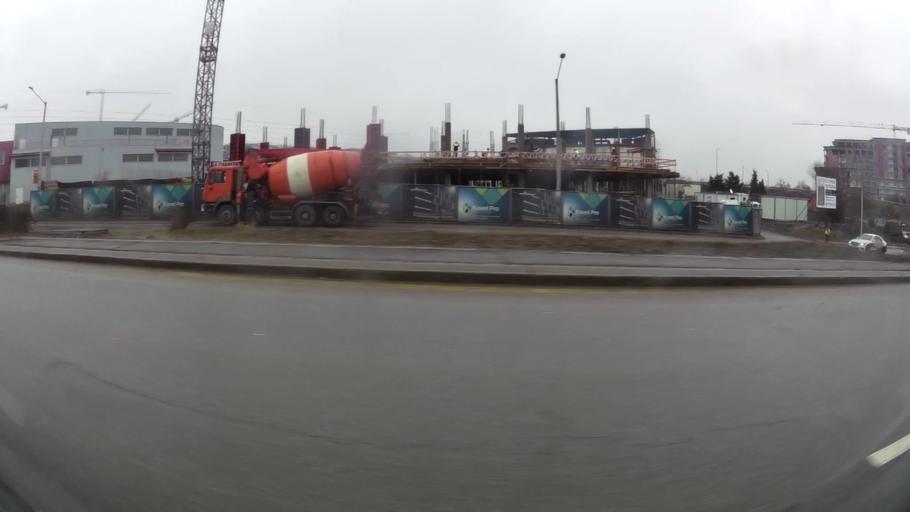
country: BG
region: Sofia-Capital
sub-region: Stolichna Obshtina
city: Sofia
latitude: 42.6249
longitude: 23.3741
